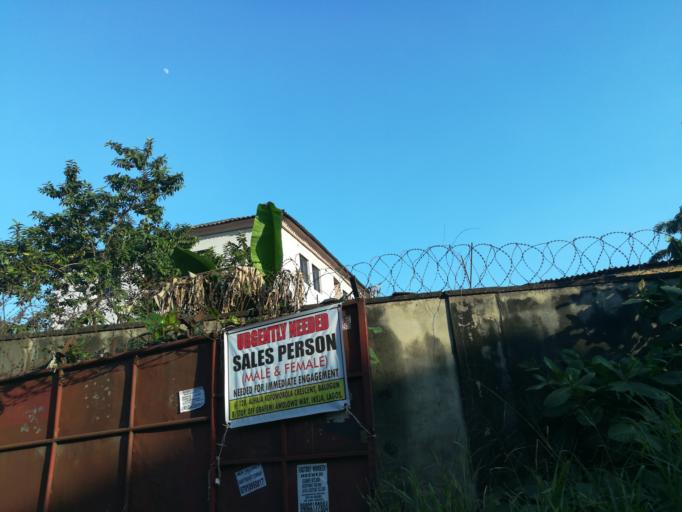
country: NG
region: Lagos
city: Ikeja
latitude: 6.6042
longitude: 3.3416
